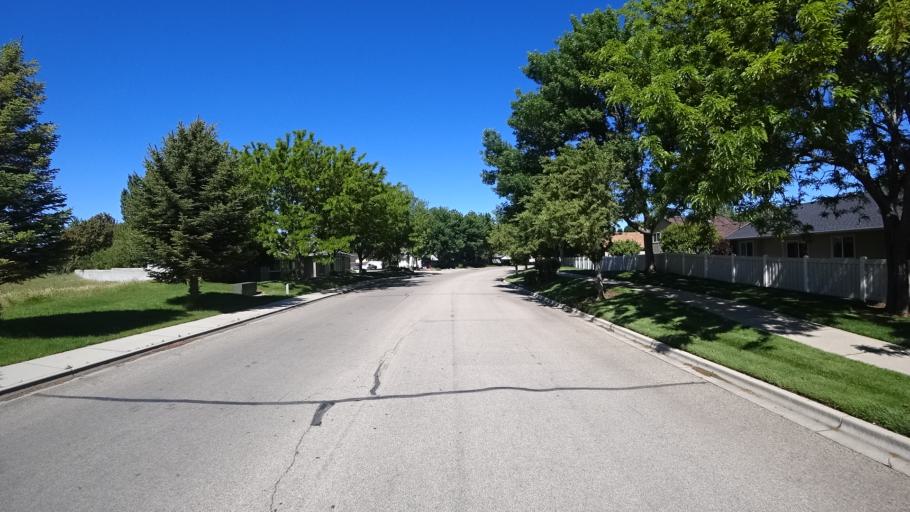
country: US
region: Idaho
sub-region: Ada County
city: Meridian
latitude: 43.6213
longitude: -116.3636
